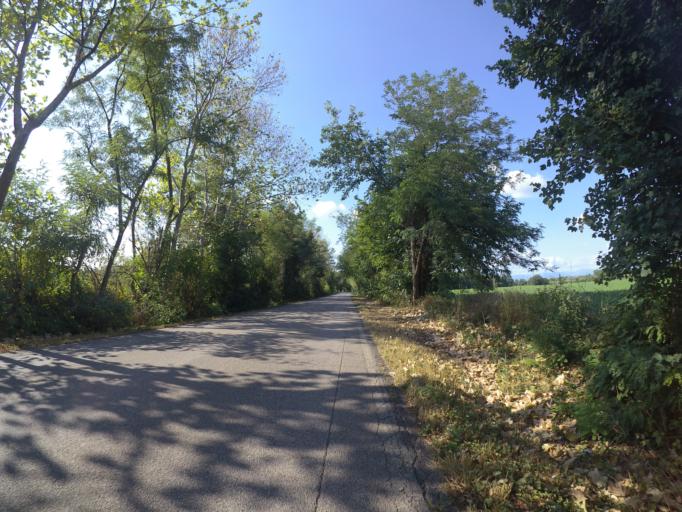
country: IT
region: Friuli Venezia Giulia
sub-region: Provincia di Udine
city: Mortegliano
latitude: 45.9596
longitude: 13.1667
